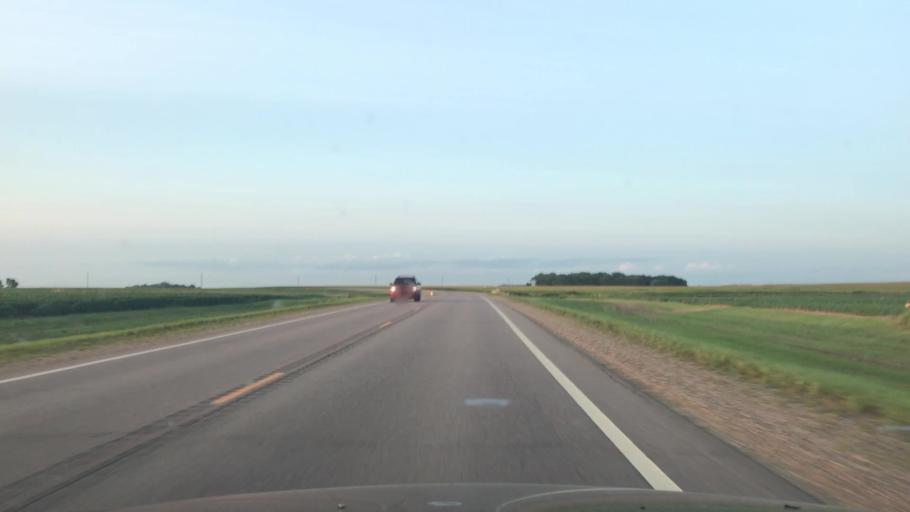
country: US
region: Minnesota
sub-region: Redwood County
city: Redwood Falls
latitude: 44.4172
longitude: -95.1218
